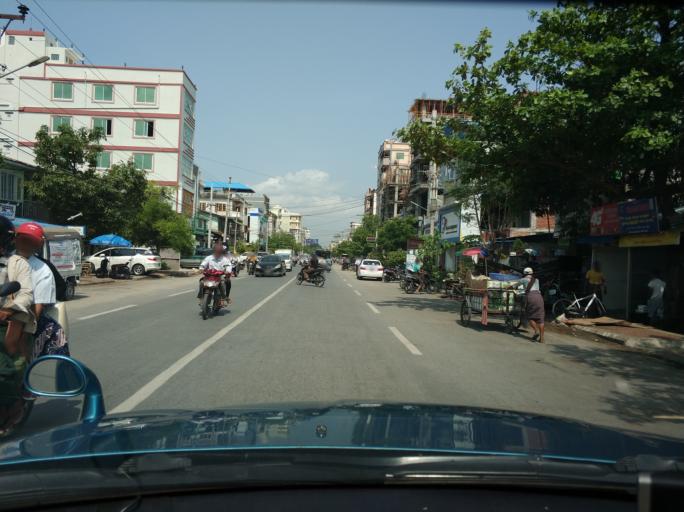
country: MM
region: Mandalay
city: Mandalay
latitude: 21.9659
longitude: 96.0898
